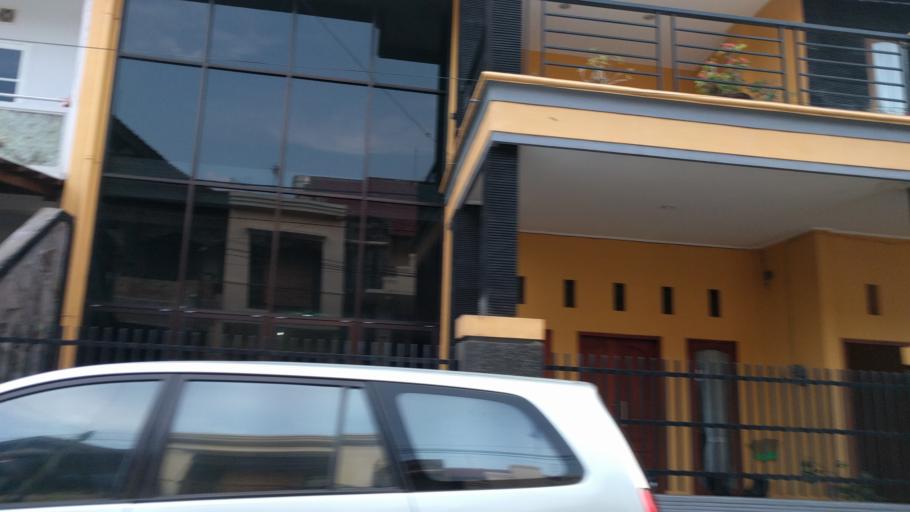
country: ID
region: Bali
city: Kuta
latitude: -8.7032
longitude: 115.1863
